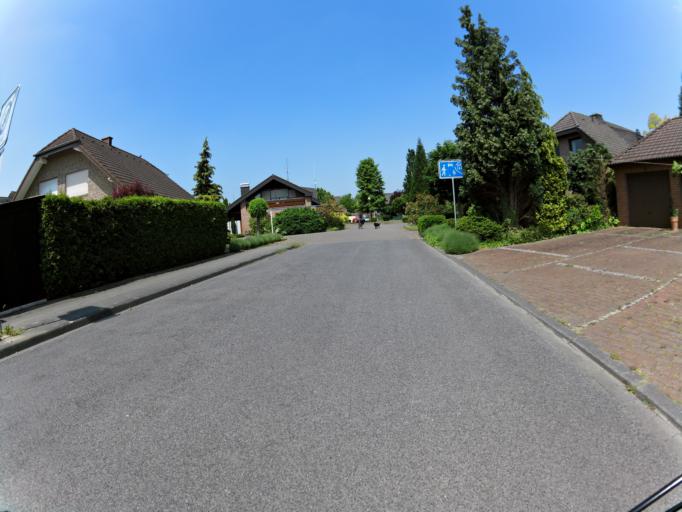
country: DE
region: North Rhine-Westphalia
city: Julich
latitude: 50.9132
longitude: 6.3646
